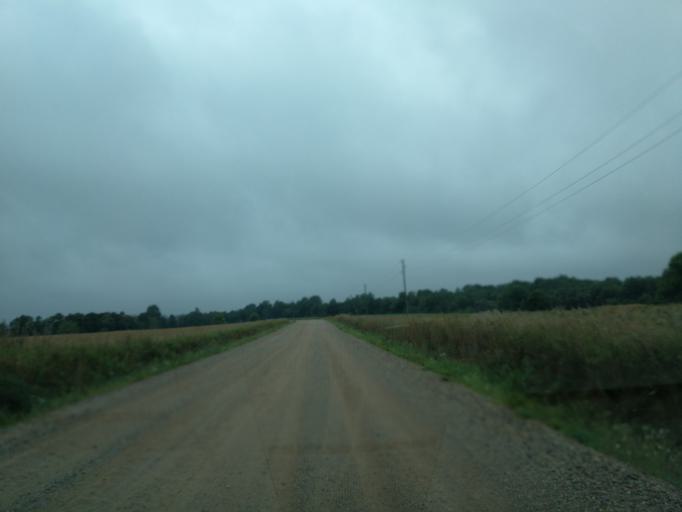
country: LV
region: Vilanu
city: Vilani
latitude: 56.3718
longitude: 27.0253
